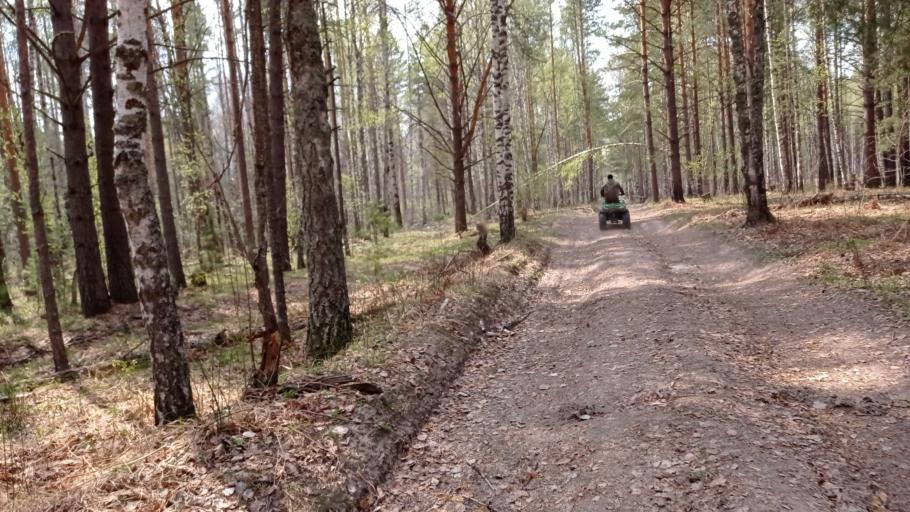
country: RU
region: Tomsk
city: Timiryazevskoye
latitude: 56.4357
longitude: 84.6503
